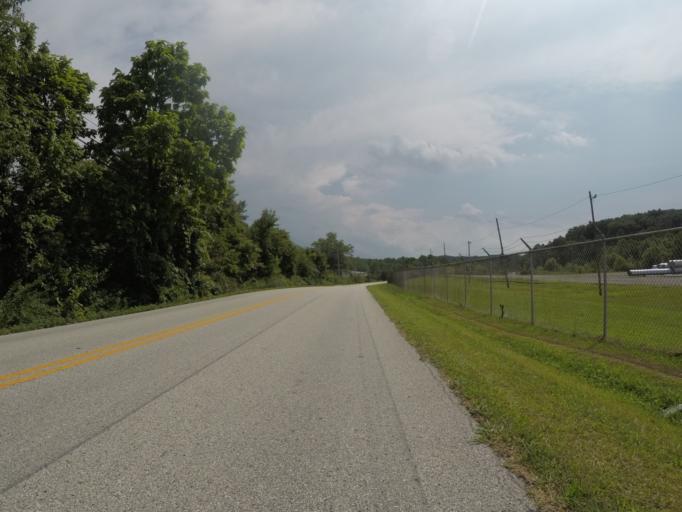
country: US
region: Kentucky
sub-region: Boyd County
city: Ironville
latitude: 38.4452
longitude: -82.7012
